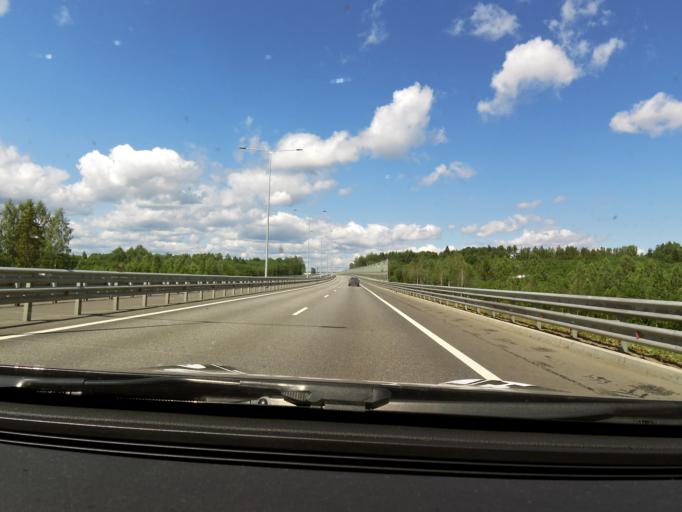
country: RU
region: Tverskaya
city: Vydropuzhsk
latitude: 57.3632
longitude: 34.6740
